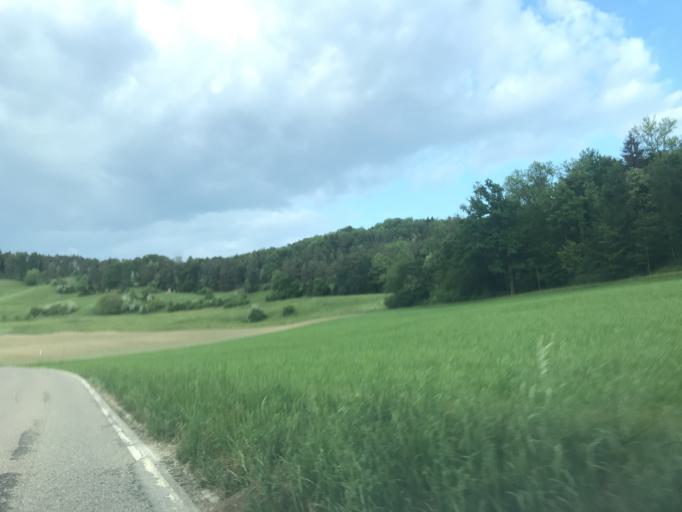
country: CH
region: Zurich
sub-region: Bezirk Winterthur
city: Wuelflingen (Kreis 6) / Oberfeld
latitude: 47.4921
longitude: 8.6869
